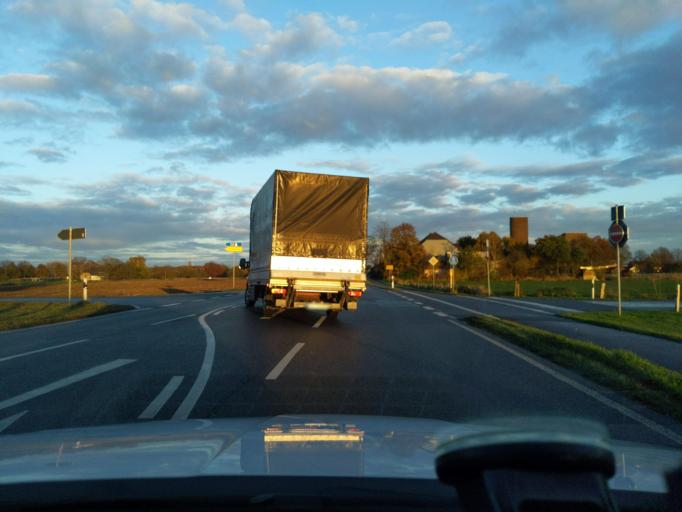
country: DE
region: North Rhine-Westphalia
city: Kalkar
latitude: 51.7079
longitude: 6.3290
